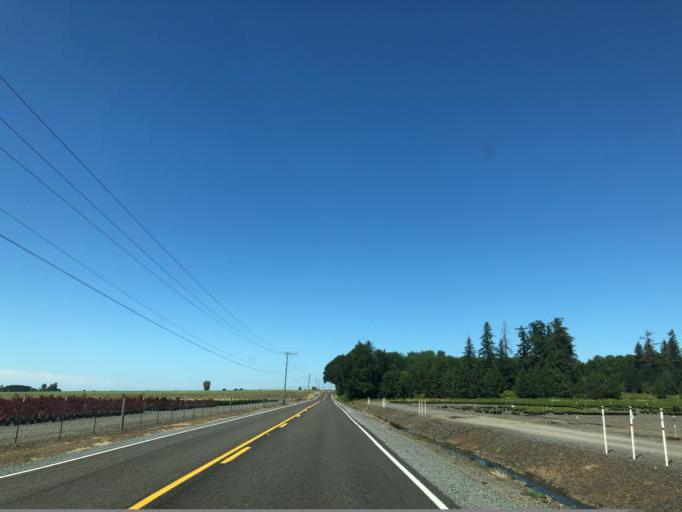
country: US
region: Oregon
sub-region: Marion County
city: Silverton
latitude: 45.0383
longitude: -122.7546
